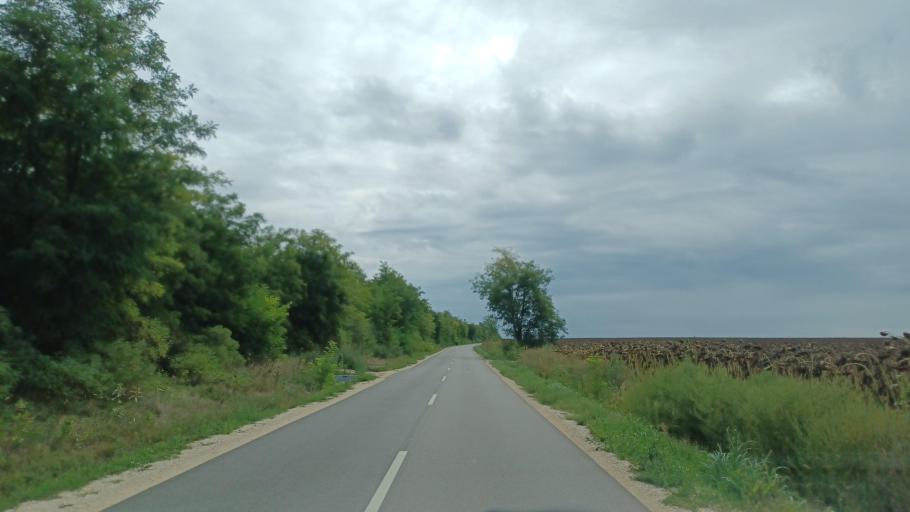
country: HU
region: Tolna
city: Szentgalpuszta
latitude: 46.4151
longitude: 18.6123
